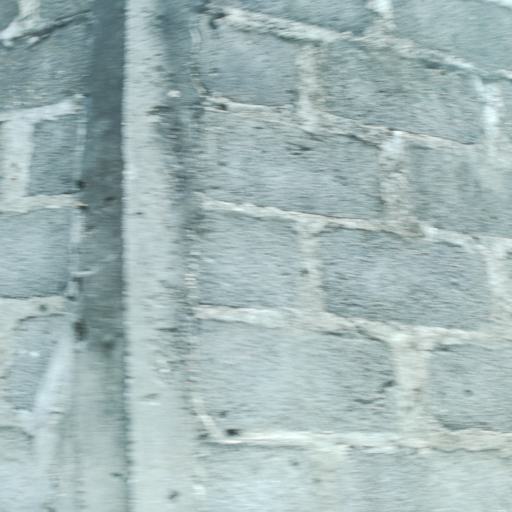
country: NG
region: Rivers
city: Port Harcourt
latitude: 4.7807
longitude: 7.0425
